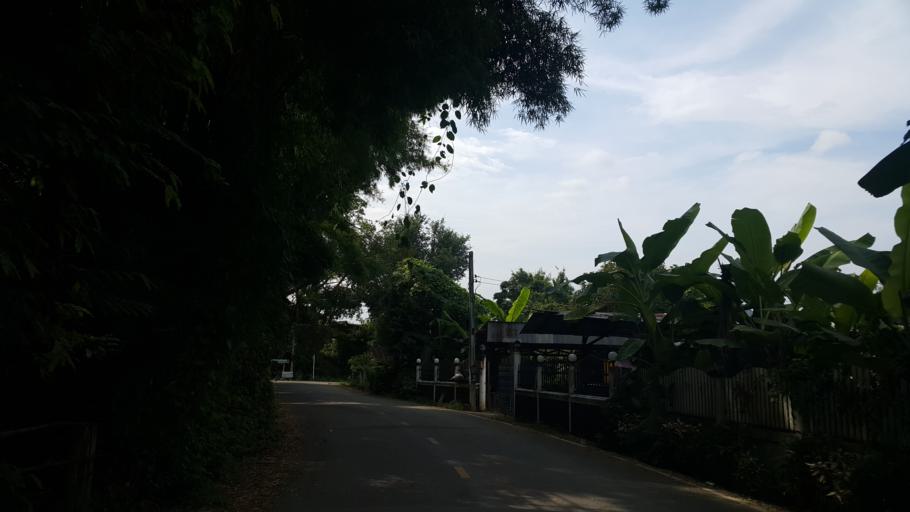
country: TH
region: Chiang Mai
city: San Sai
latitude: 18.9075
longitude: 99.1271
